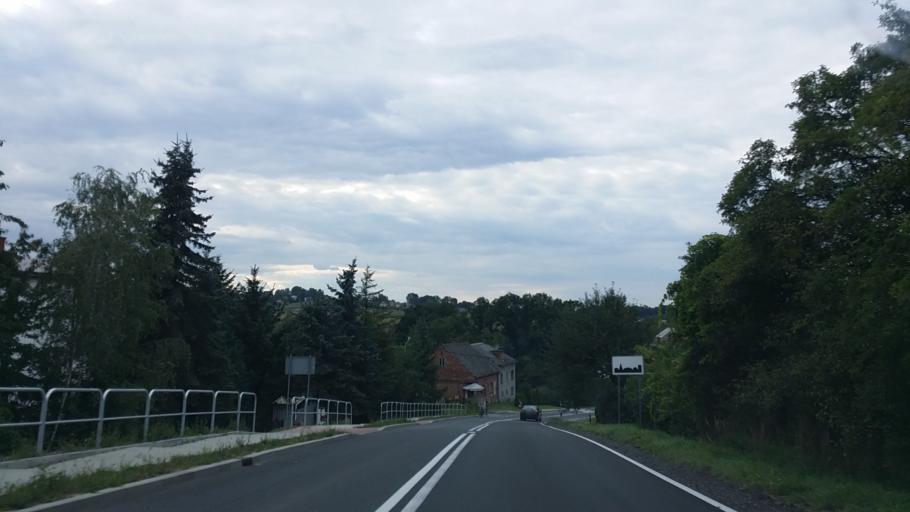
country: PL
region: Lesser Poland Voivodeship
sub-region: Powiat wadowicki
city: Ryczow
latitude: 49.9729
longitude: 19.5628
